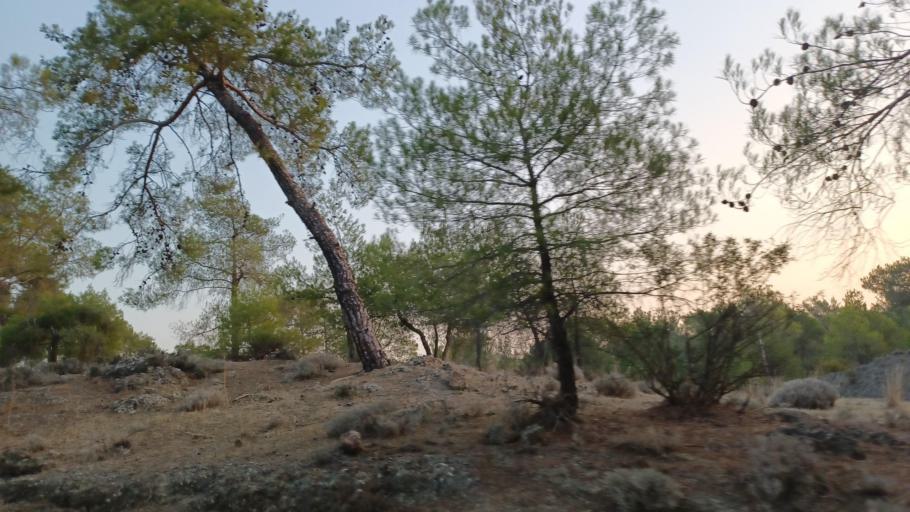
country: CY
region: Larnaka
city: Kornos
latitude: 34.9088
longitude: 33.3564
